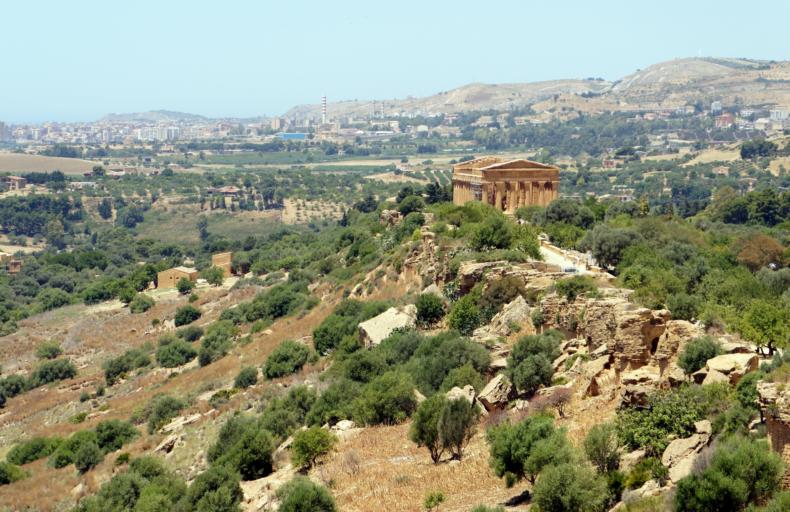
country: IT
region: Sicily
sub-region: Agrigento
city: San Leone Mose
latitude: 37.2889
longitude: 13.5989
